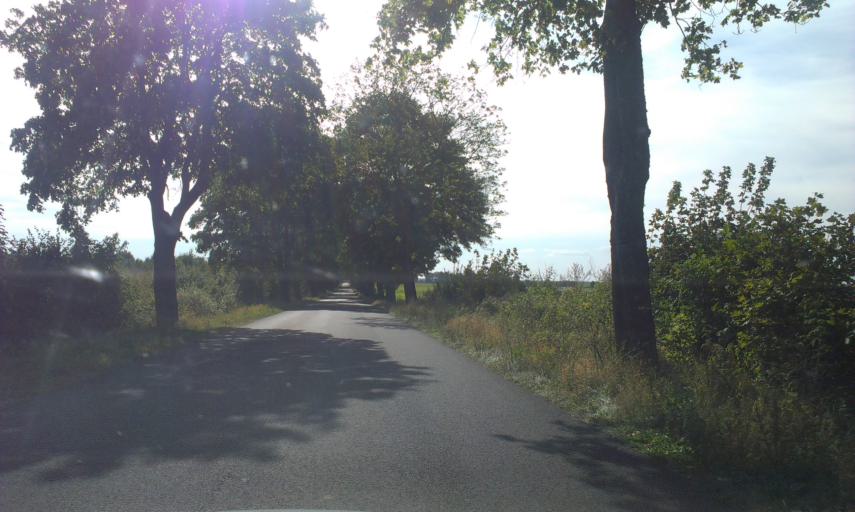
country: PL
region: Greater Poland Voivodeship
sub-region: Powiat zlotowski
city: Zlotow
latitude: 53.4665
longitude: 16.9882
